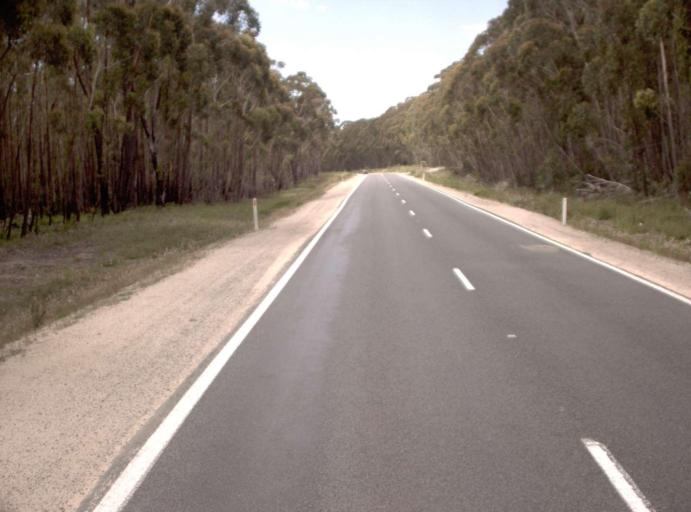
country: AU
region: New South Wales
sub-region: Bega Valley
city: Eden
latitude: -37.5351
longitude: 149.4792
